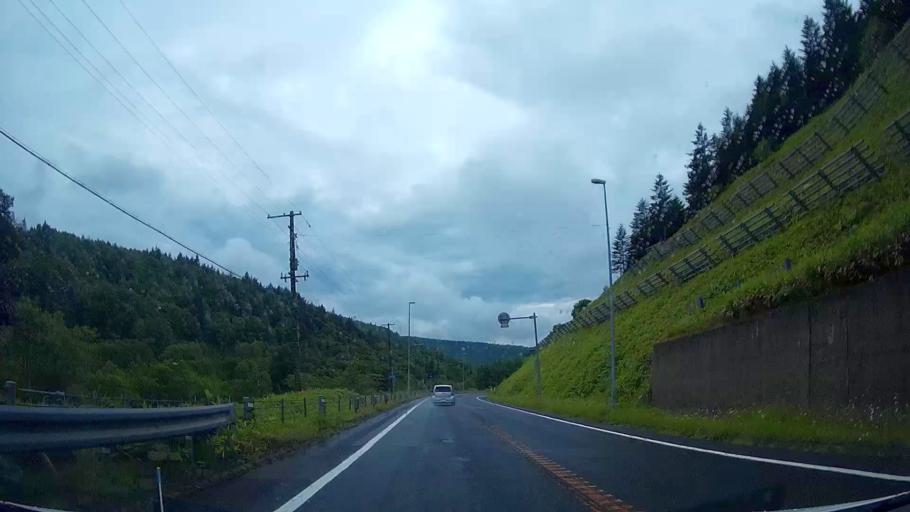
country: JP
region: Hokkaido
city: Shiraoi
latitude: 42.7041
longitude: 141.1688
